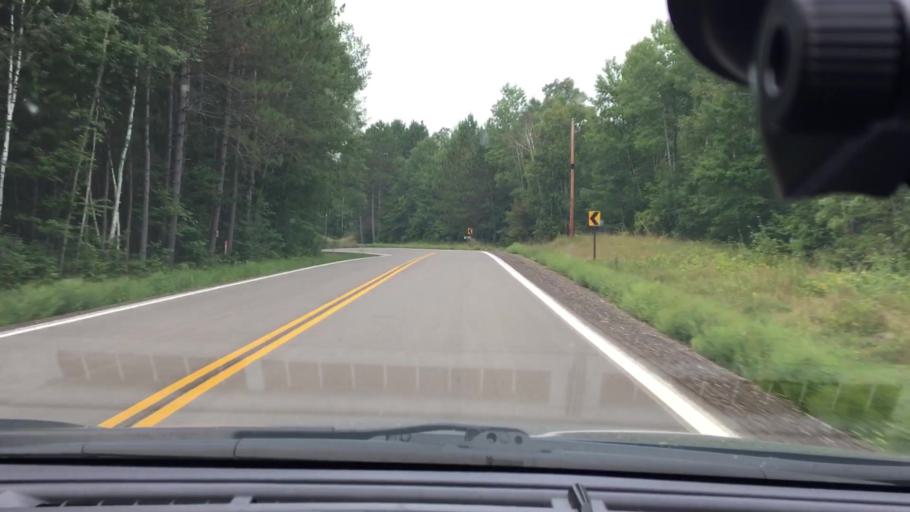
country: US
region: Minnesota
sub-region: Crow Wing County
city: Cross Lake
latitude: 46.6587
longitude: -93.9735
